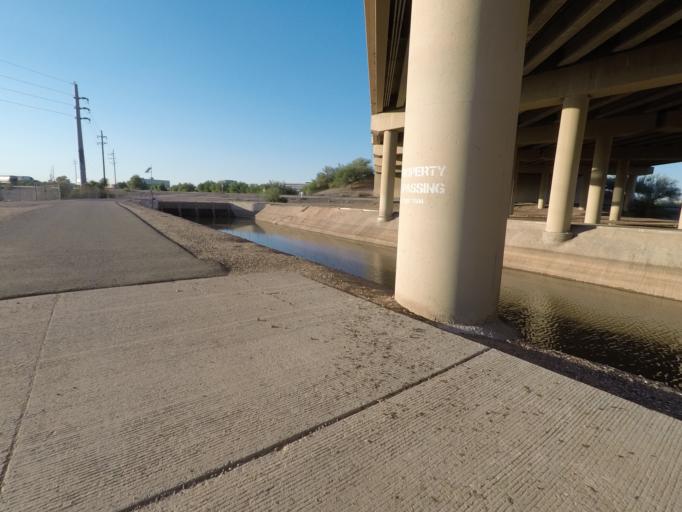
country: US
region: Arizona
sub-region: Maricopa County
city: Tempe Junction
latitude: 33.4431
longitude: -111.9808
